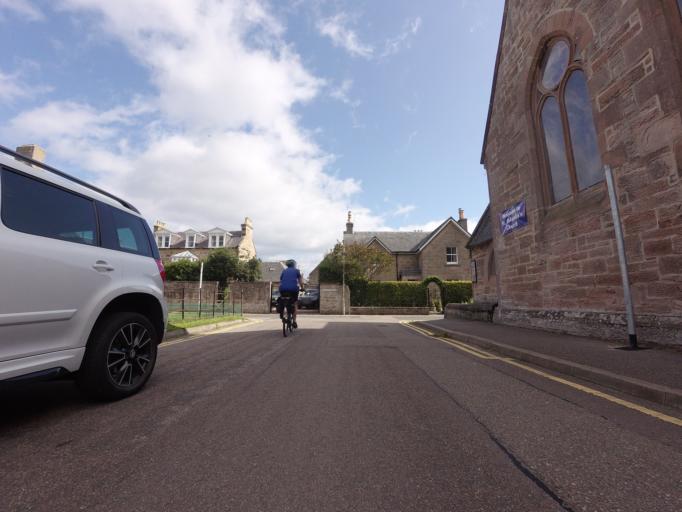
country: GB
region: Scotland
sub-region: Highland
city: Nairn
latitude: 57.5826
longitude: -3.8692
